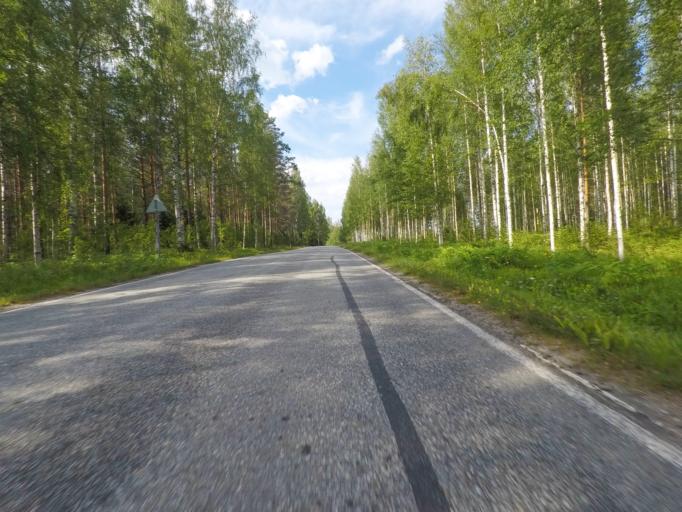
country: FI
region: Southern Savonia
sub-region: Mikkeli
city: Puumala
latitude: 61.7051
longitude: 28.2110
